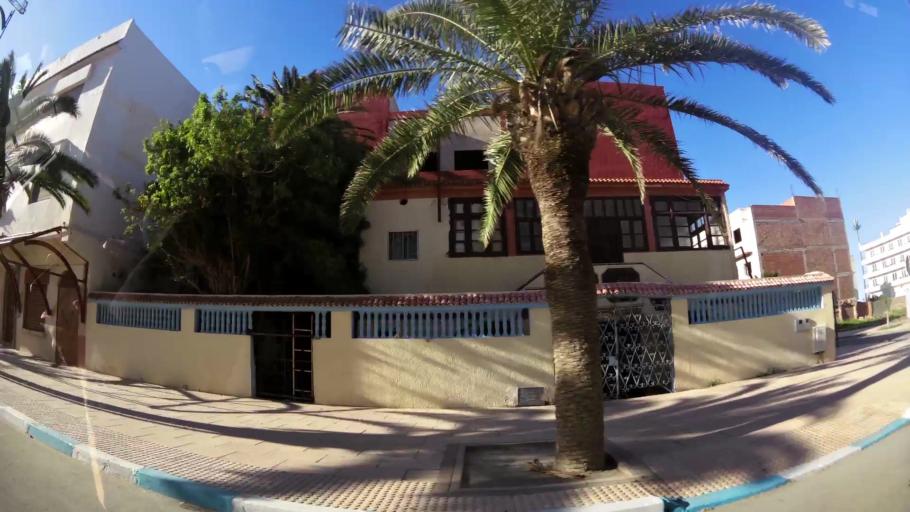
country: MA
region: Oriental
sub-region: Berkane-Taourirt
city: Madagh
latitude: 35.0857
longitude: -2.2244
